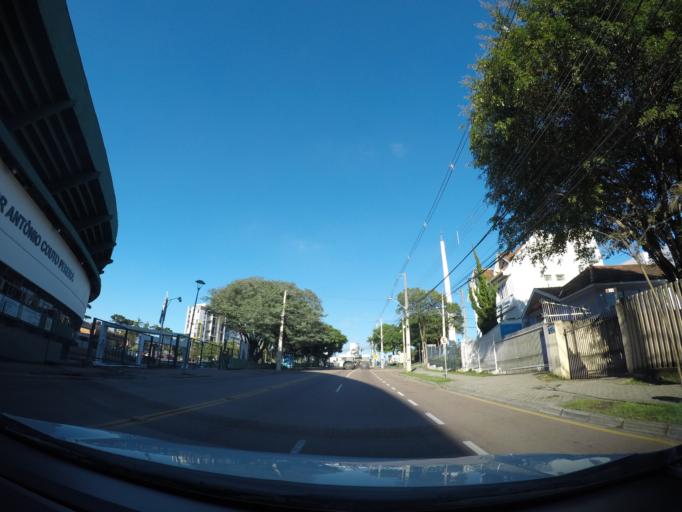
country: BR
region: Parana
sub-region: Curitiba
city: Curitiba
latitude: -25.4205
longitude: -49.2606
